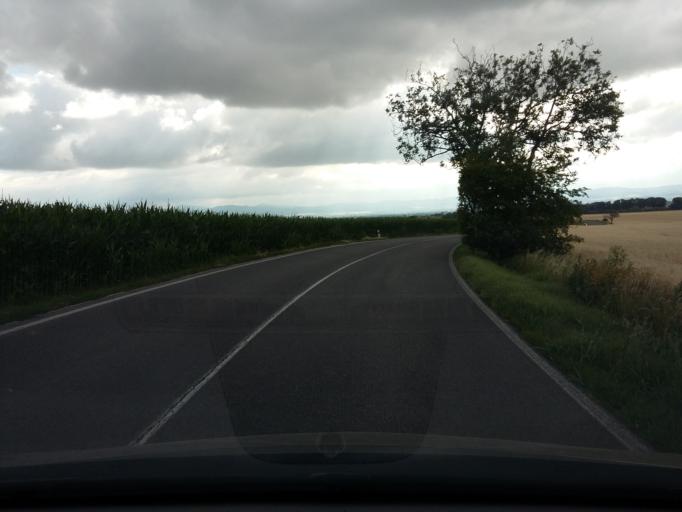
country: SK
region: Trnavsky
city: Vrbove
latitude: 48.6014
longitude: 17.6920
